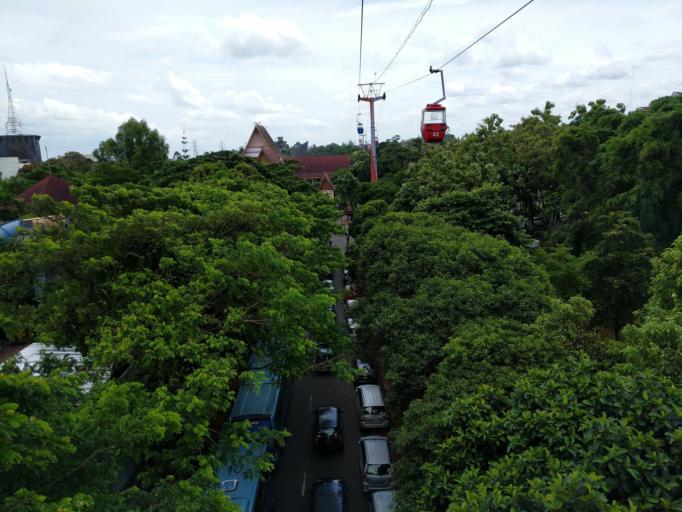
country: ID
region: Jakarta Raya
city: Jakarta
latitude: -6.3005
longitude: 106.8914
